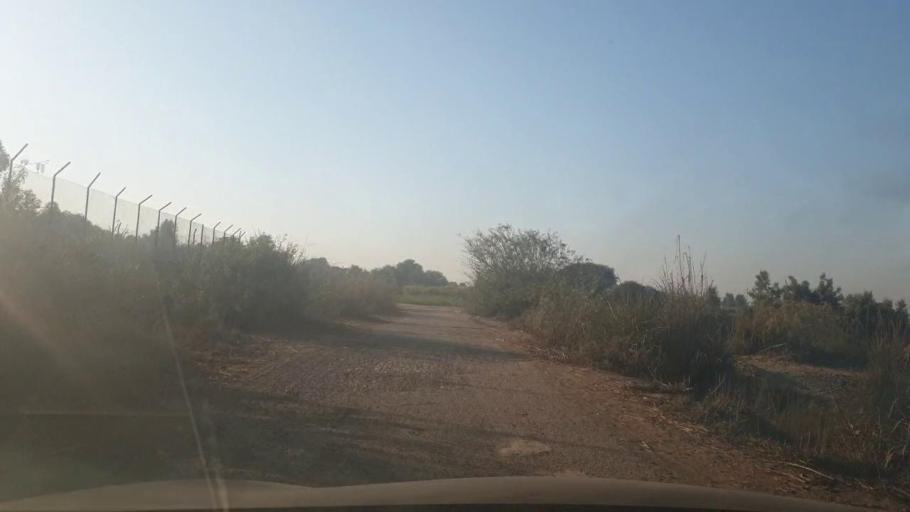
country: PK
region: Sindh
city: Ghotki
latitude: 28.0963
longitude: 69.3638
